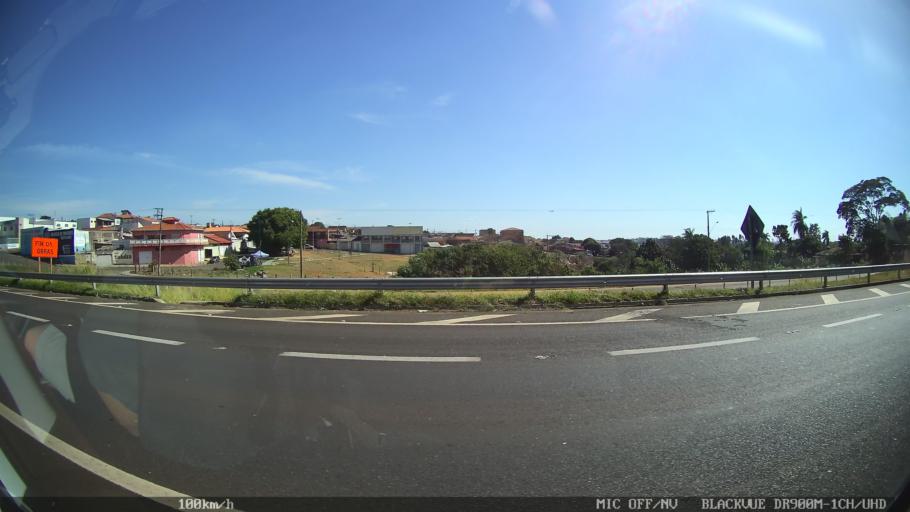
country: BR
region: Sao Paulo
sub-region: Franca
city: Franca
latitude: -20.5274
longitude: -47.4219
